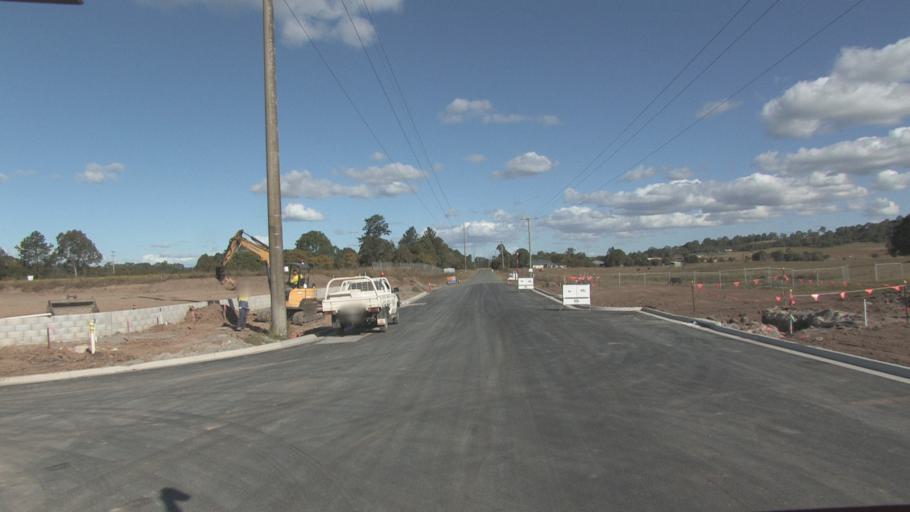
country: AU
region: Queensland
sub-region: Logan
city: Logan Reserve
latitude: -27.7191
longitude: 153.1148
